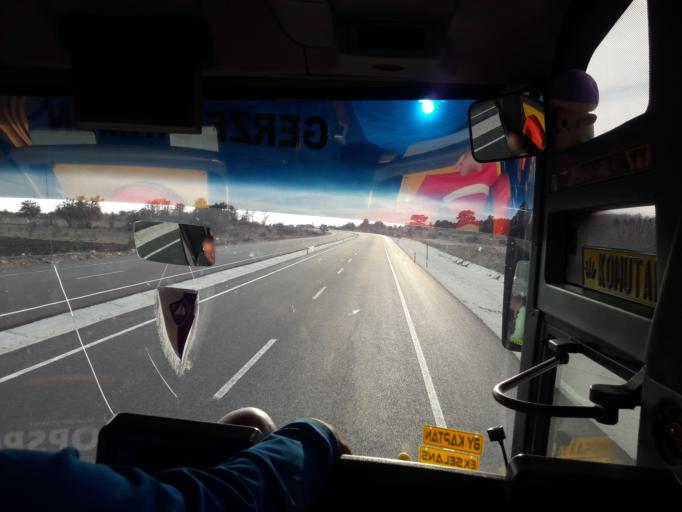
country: TR
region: Cankiri
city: Ilgaz
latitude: 40.8589
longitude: 33.6200
